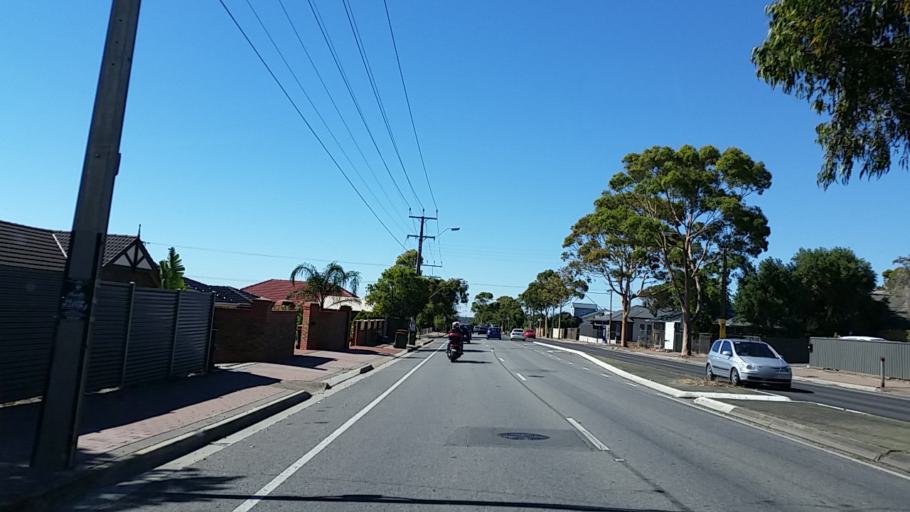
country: AU
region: South Australia
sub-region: Adelaide Hills
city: Seacliff
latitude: -35.0349
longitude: 138.5243
